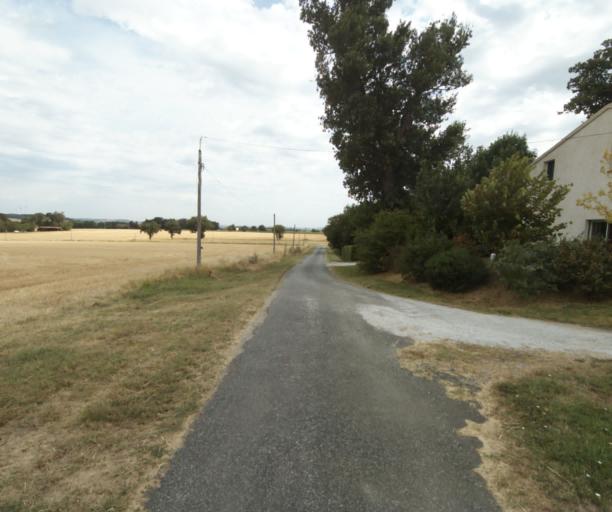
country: FR
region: Midi-Pyrenees
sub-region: Departement de la Haute-Garonne
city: Saint-Felix-Lauragais
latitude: 43.4323
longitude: 1.9257
